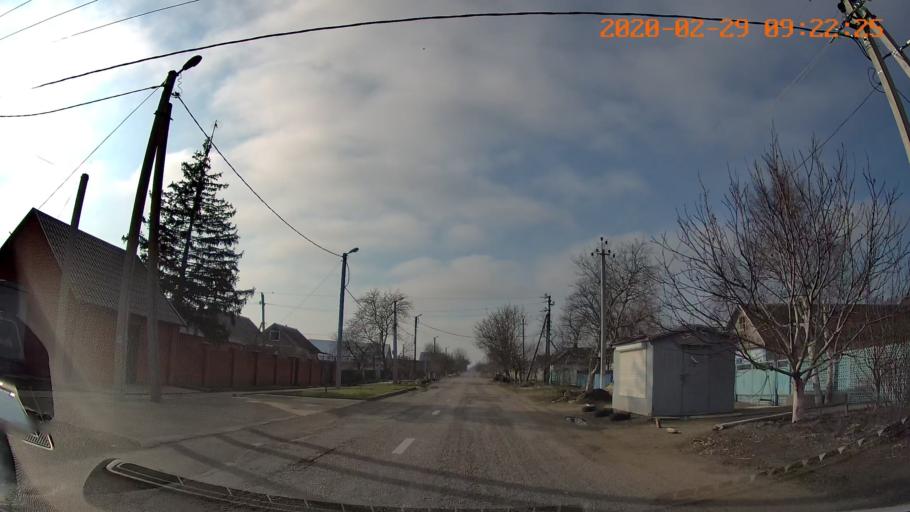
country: MD
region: Telenesti
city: Pervomaisc
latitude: 46.7354
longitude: 29.9641
